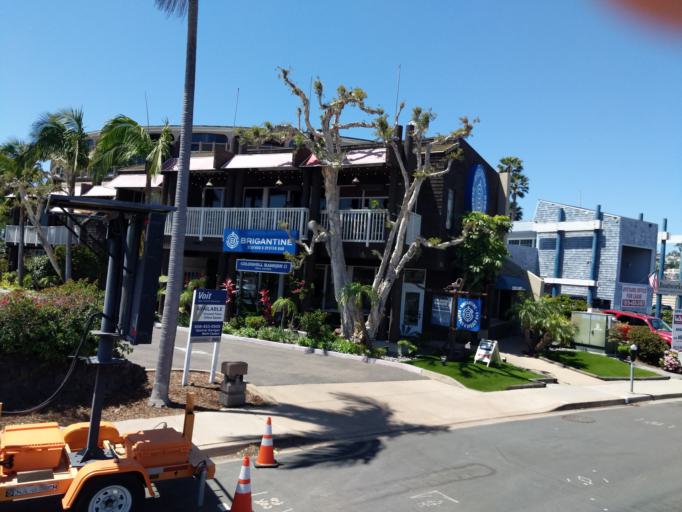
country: US
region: California
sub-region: San Diego County
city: Coronado
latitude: 32.7211
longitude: -117.2282
